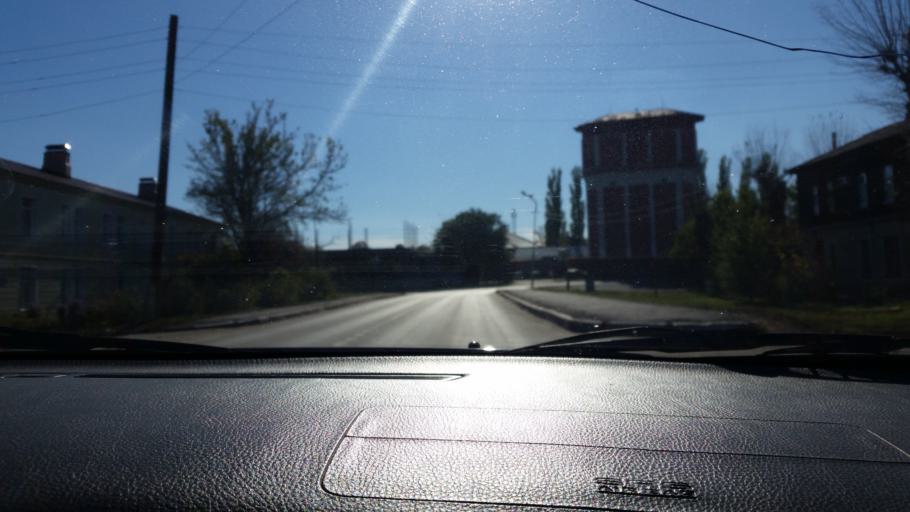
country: RU
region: Lipetsk
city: Gryazi
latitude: 52.4872
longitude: 39.9544
